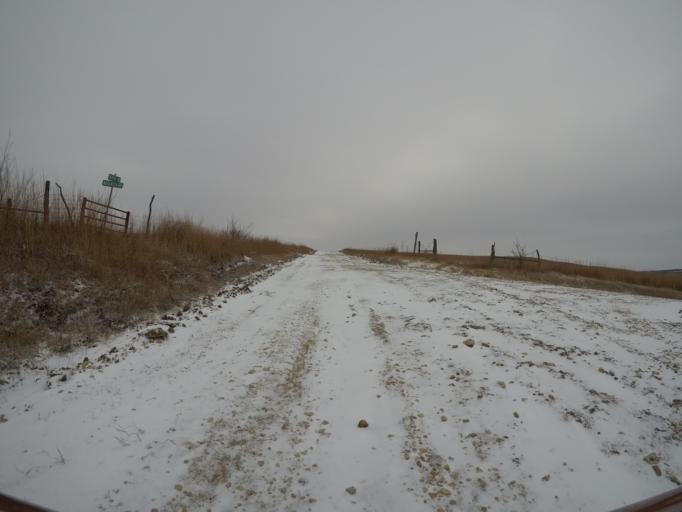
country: US
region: Kansas
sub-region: Wabaunsee County
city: Alma
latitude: 38.8700
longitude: -96.1135
